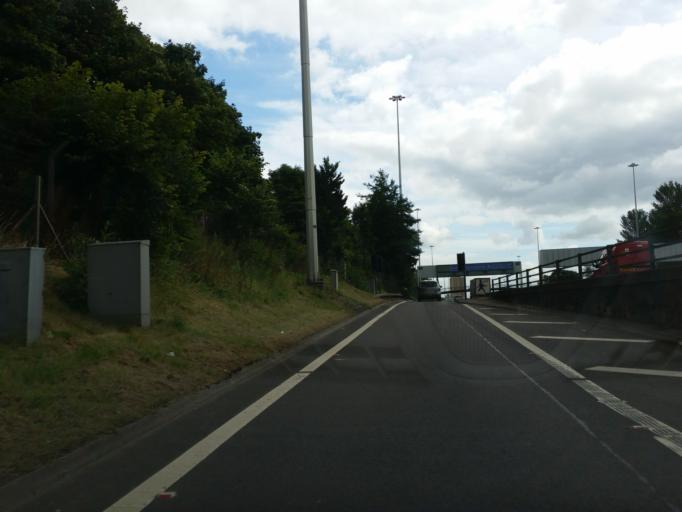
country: GB
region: Scotland
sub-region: Glasgow City
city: Glasgow
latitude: 55.8702
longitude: -4.2490
